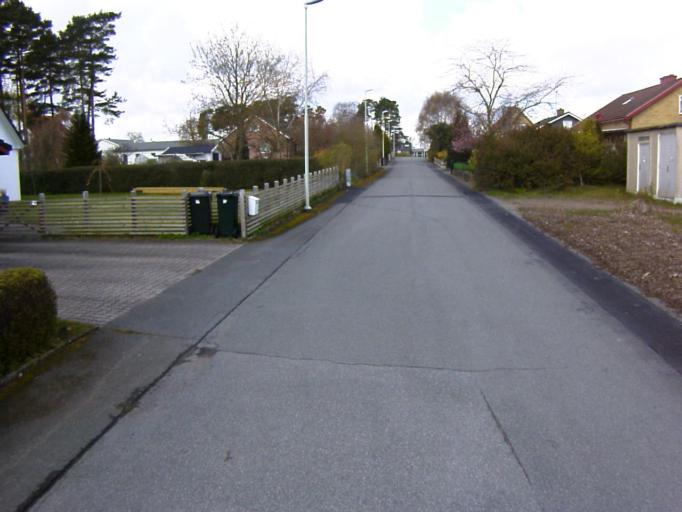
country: SE
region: Skane
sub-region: Kristianstads Kommun
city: Kristianstad
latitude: 56.0112
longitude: 14.1009
